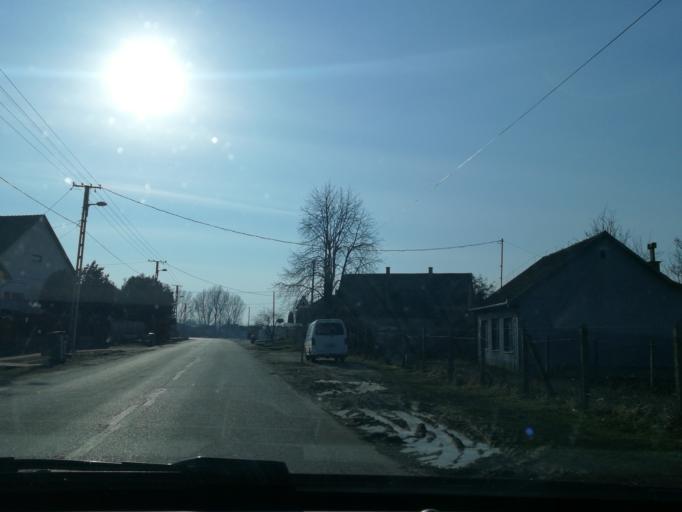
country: HU
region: Szabolcs-Szatmar-Bereg
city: Levelek
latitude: 48.0429
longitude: 21.9793
